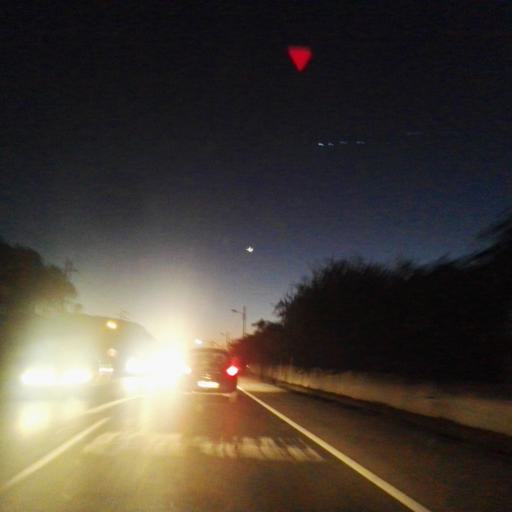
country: PT
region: Santarem
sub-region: Cartaxo
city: Pontevel
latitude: 39.1094
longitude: -8.8333
